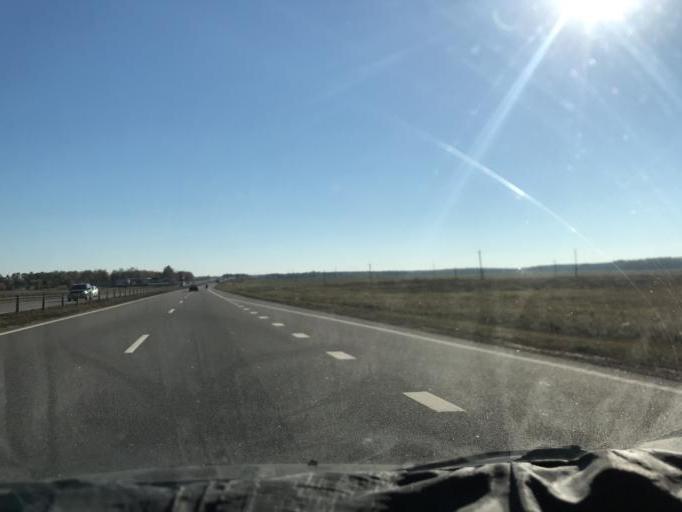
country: BY
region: Mogilev
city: Yalizava
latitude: 53.2205
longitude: 29.0231
